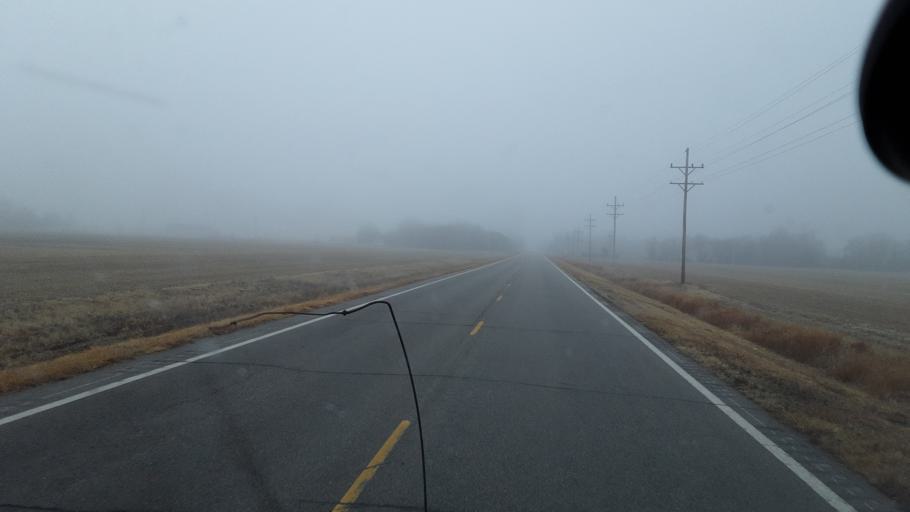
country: US
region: Kansas
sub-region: Reno County
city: South Hutchinson
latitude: 37.9590
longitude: -97.9401
